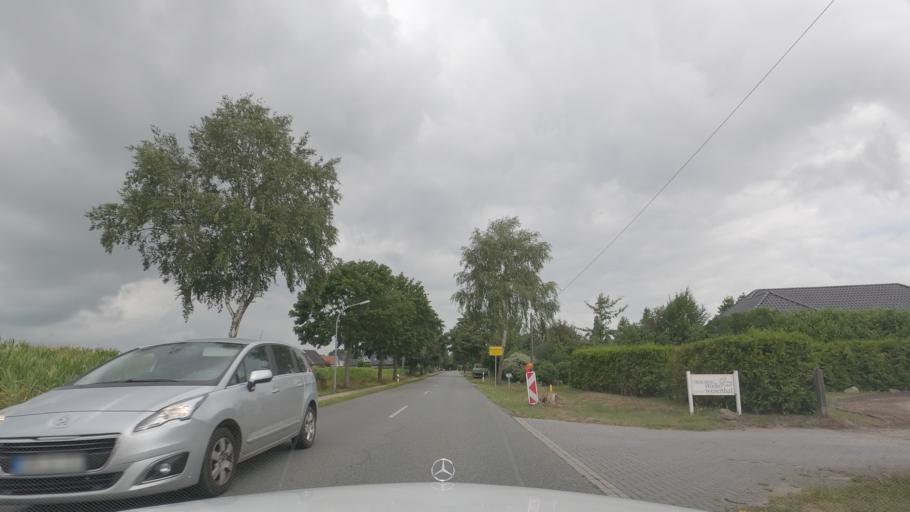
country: DE
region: Lower Saxony
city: Neuenkirchen
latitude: 53.2275
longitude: 8.5312
